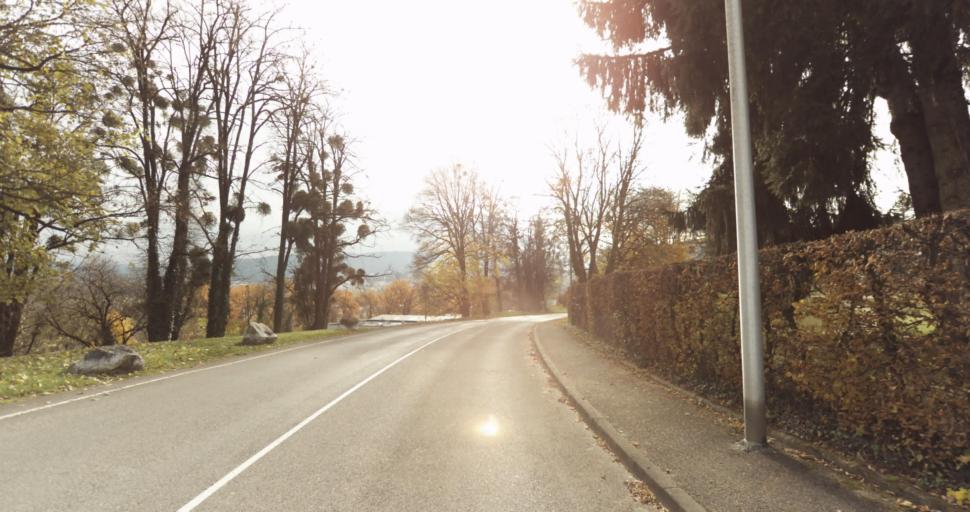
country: FR
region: Rhone-Alpes
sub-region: Departement de la Haute-Savoie
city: Meythet
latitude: 45.9172
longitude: 6.0972
